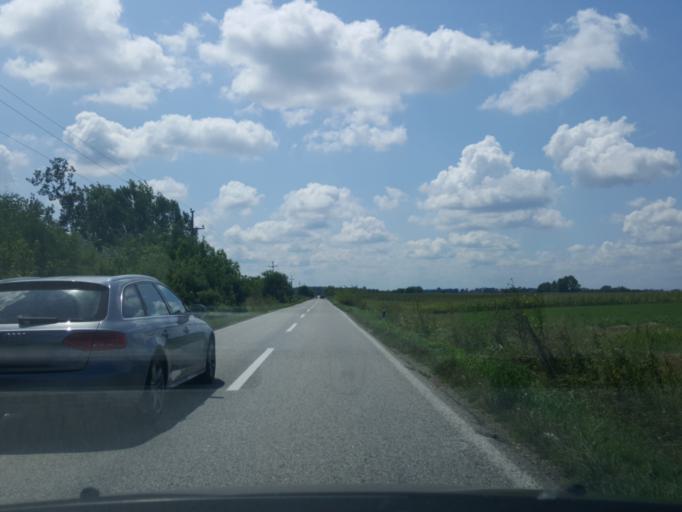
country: RS
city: Metkovic
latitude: 44.8727
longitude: 19.5498
